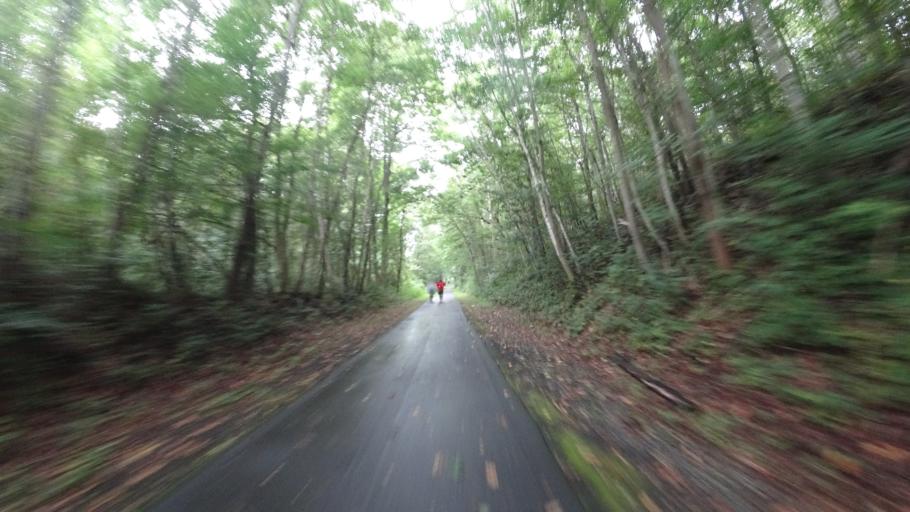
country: BE
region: Wallonia
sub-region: Province de Namur
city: Namur
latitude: 50.4899
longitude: 4.8597
